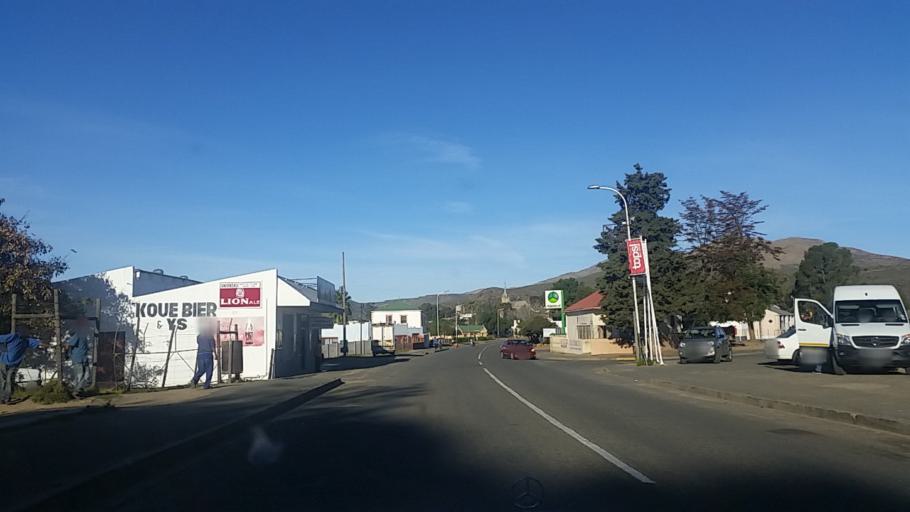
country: ZA
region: Western Cape
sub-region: Eden District Municipality
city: Knysna
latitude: -33.6589
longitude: 23.1182
